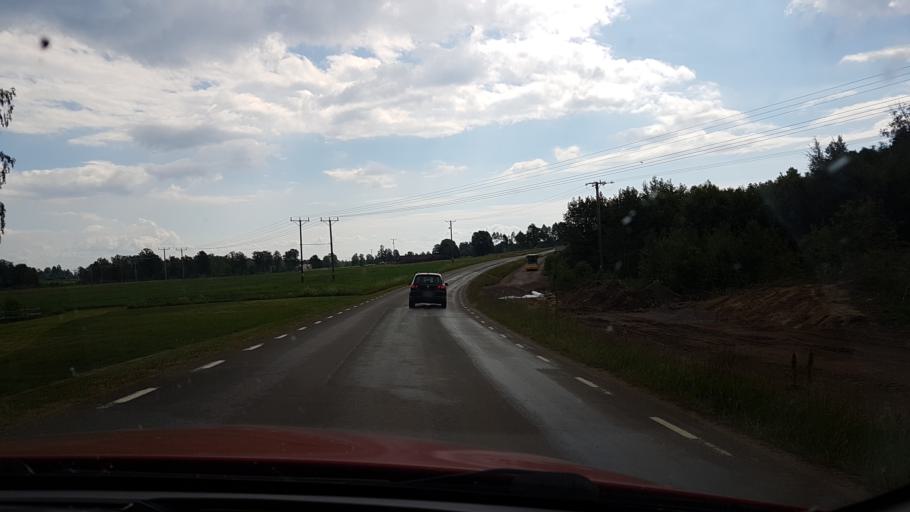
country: SE
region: Vaestra Goetaland
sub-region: Hjo Kommun
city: Hjo
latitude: 58.3081
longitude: 14.2315
